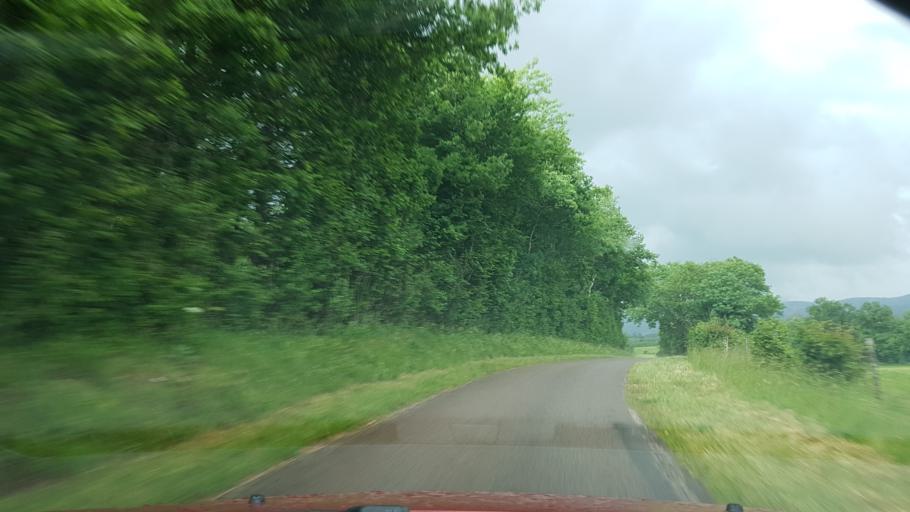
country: FR
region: Franche-Comte
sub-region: Departement du Jura
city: Clairvaux-les-Lacs
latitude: 46.5316
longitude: 5.7179
